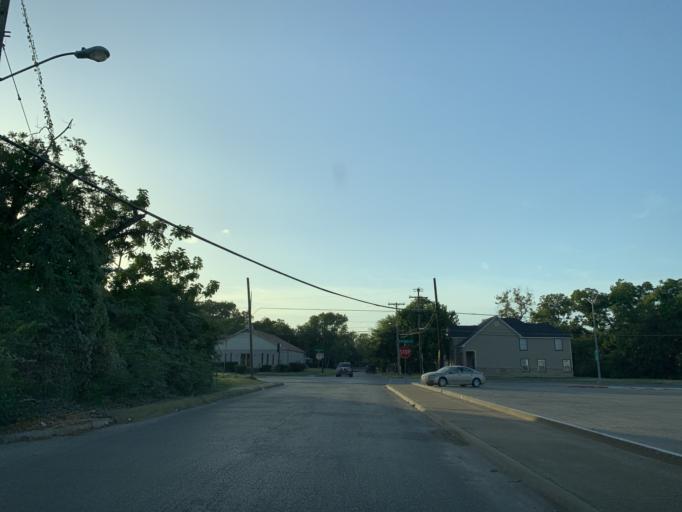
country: US
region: Texas
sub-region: Dallas County
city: Dallas
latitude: 32.7601
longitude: -96.7471
